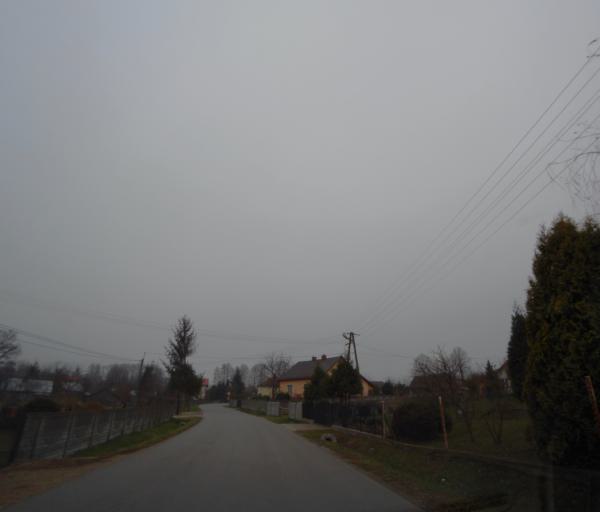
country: PL
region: Subcarpathian Voivodeship
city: Nowa Sarzyna
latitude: 50.2894
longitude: 22.3533
